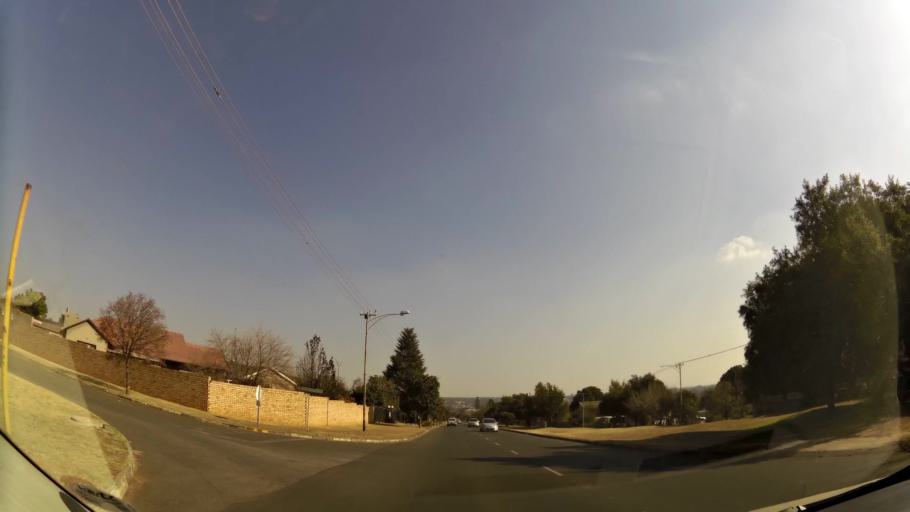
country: ZA
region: Gauteng
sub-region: West Rand District Municipality
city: Randfontein
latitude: -26.1567
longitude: 27.6982
